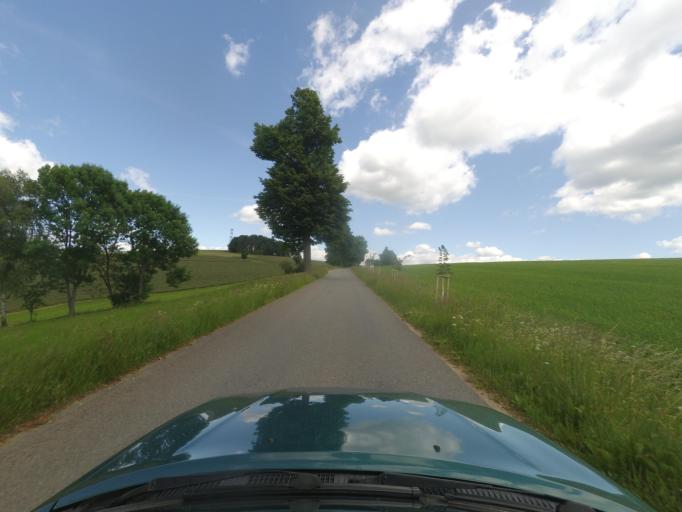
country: CZ
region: Pardubicky
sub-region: Okres Usti nad Orlici
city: Kunvald
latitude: 50.1157
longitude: 16.5750
